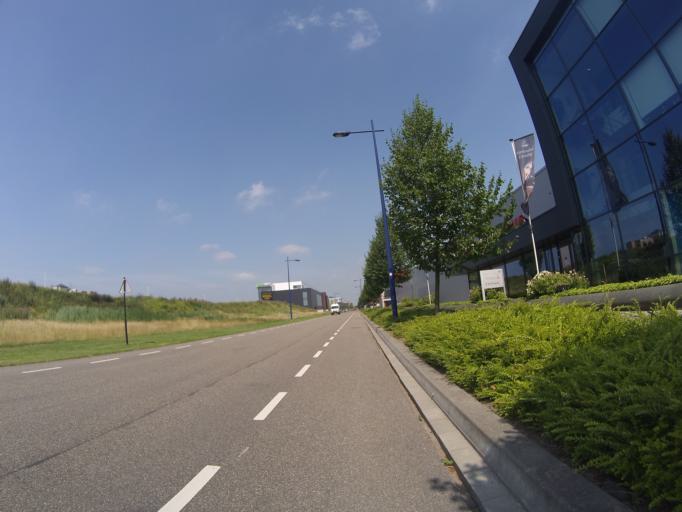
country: NL
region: Utrecht
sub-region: Gemeente Amersfoort
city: Hoogland
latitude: 52.1891
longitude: 5.4120
